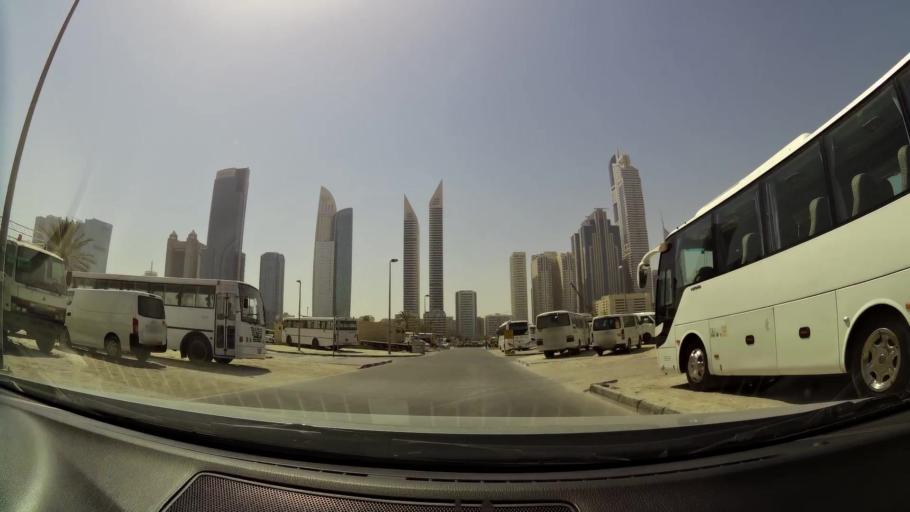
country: AE
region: Ash Shariqah
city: Sharjah
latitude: 25.2262
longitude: 55.2769
